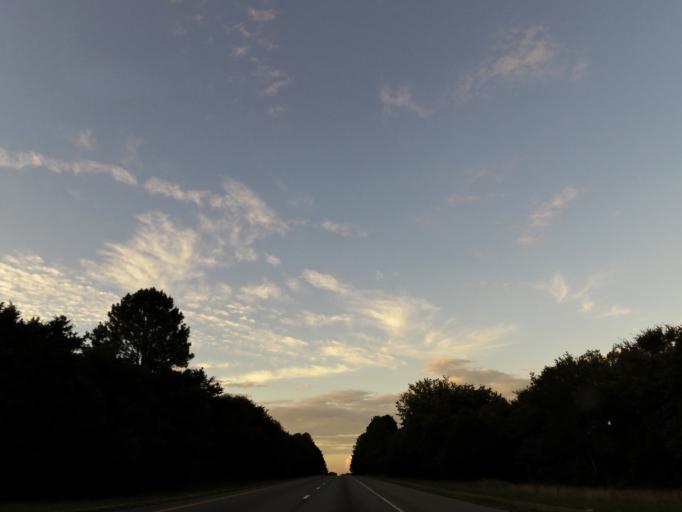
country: US
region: Tennessee
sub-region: McMinn County
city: Athens
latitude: 35.4947
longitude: -84.6195
